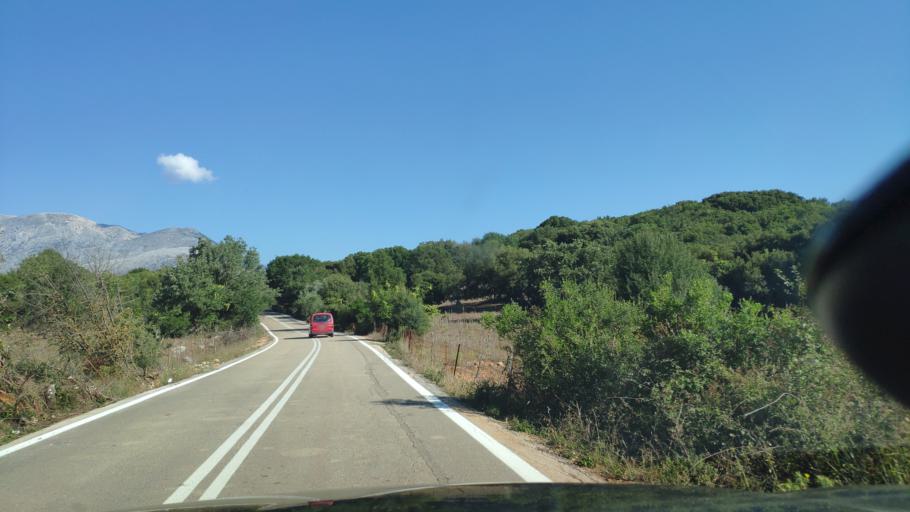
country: GR
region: West Greece
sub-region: Nomos Aitolias kai Akarnanias
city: Fitiai
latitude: 38.6867
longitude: 21.1179
